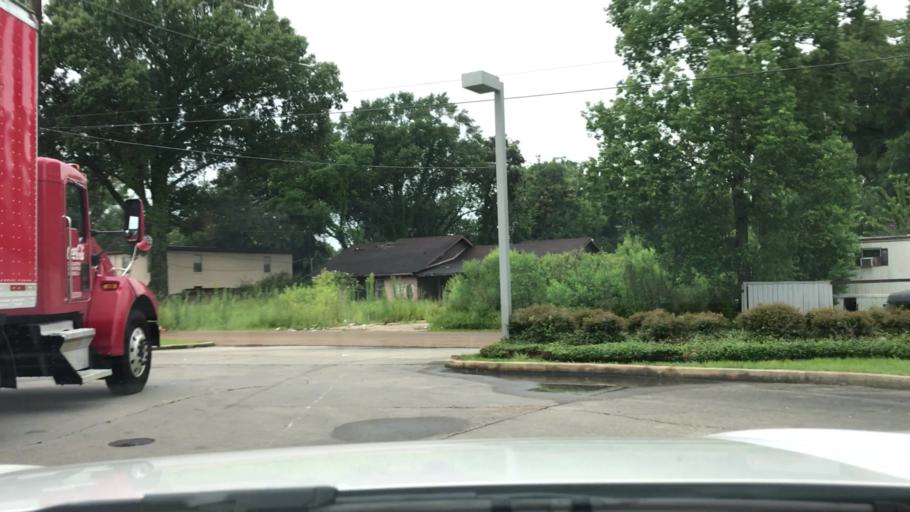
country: US
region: Louisiana
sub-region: East Baton Rouge Parish
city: Merrydale
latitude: 30.4822
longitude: -91.1174
